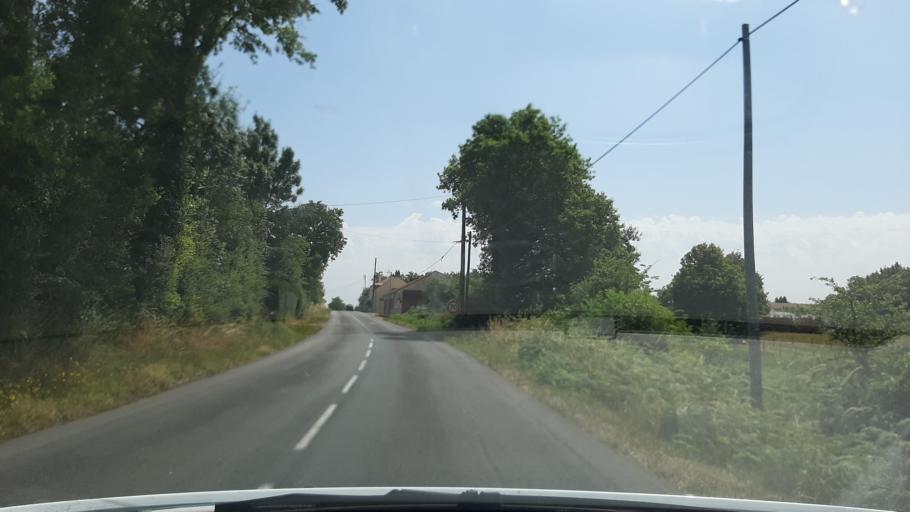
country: FR
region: Pays de la Loire
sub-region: Departement de la Vendee
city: Le Poire-sur-Vie
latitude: 46.7838
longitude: -1.5447
